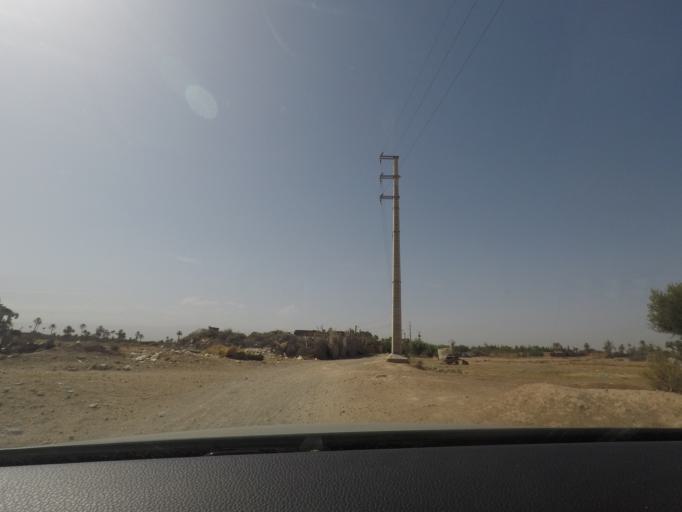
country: MA
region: Marrakech-Tensift-Al Haouz
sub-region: Marrakech
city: Marrakesh
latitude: 31.5764
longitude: -8.0260
